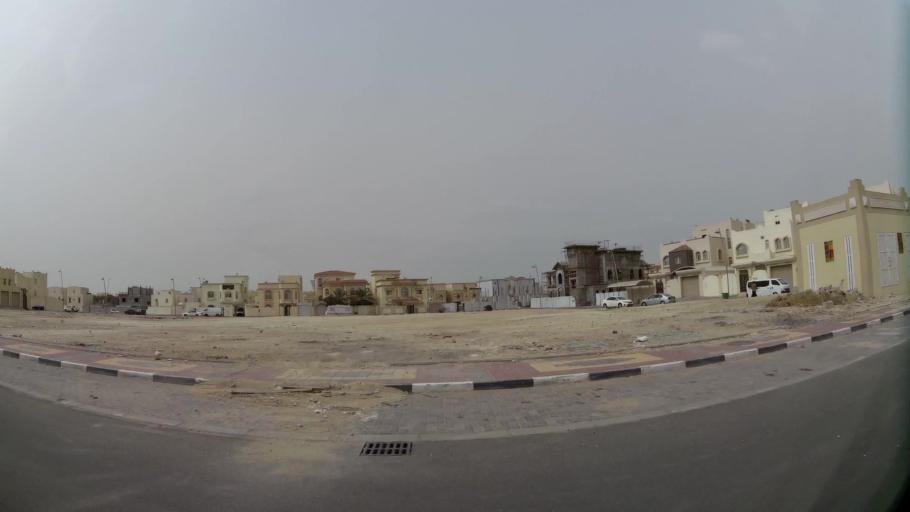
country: QA
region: Baladiyat ad Dawhah
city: Doha
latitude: 25.2325
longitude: 51.5507
